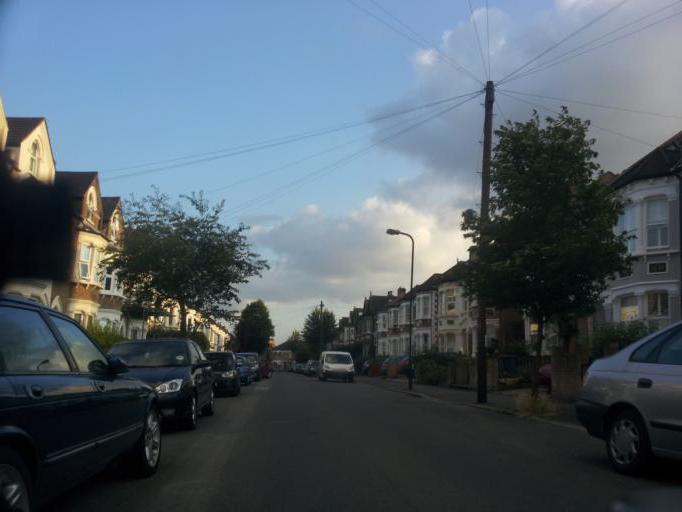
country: GB
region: England
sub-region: Greater London
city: Beckenham
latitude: 51.4226
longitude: -0.0552
